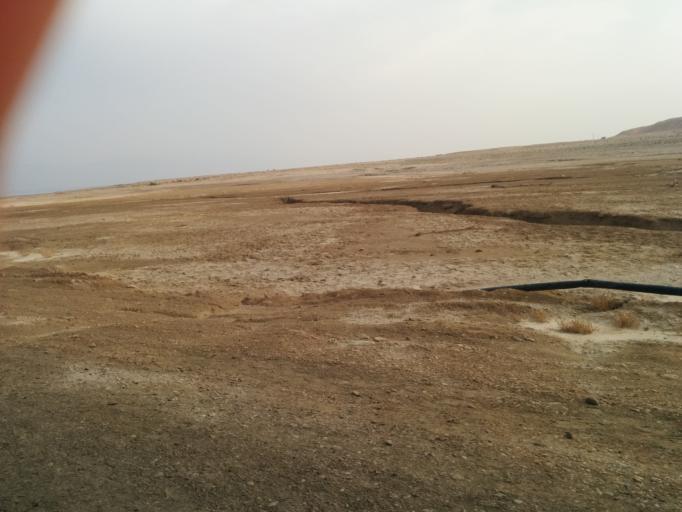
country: PS
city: `Arab ar Rashaydah
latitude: 31.4198
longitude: 35.3835
